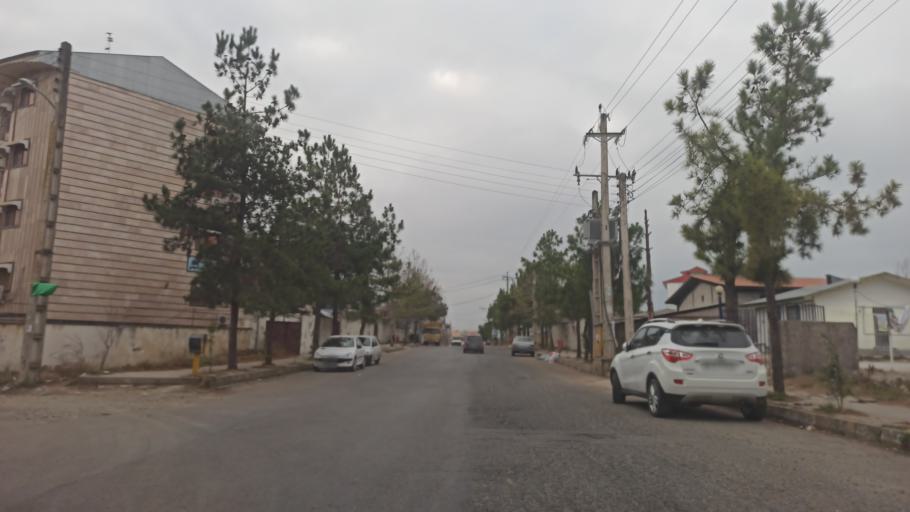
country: IR
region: Gilan
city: Fuman
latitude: 37.2309
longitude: 49.3127
